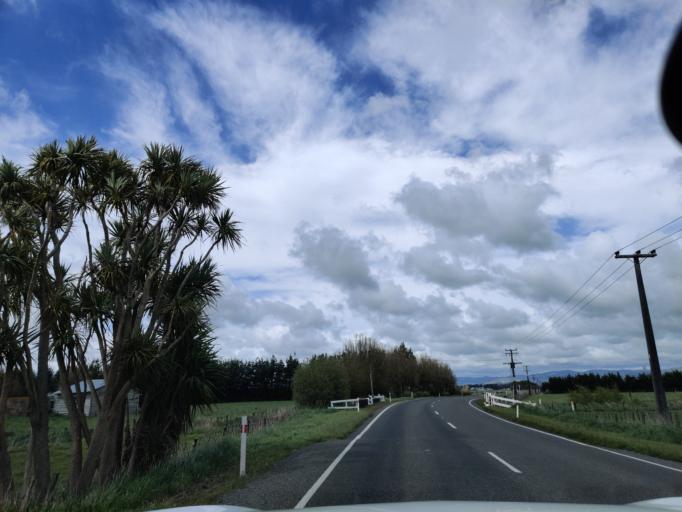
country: NZ
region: Manawatu-Wanganui
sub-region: Palmerston North City
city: Palmerston North
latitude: -40.3286
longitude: 175.5088
